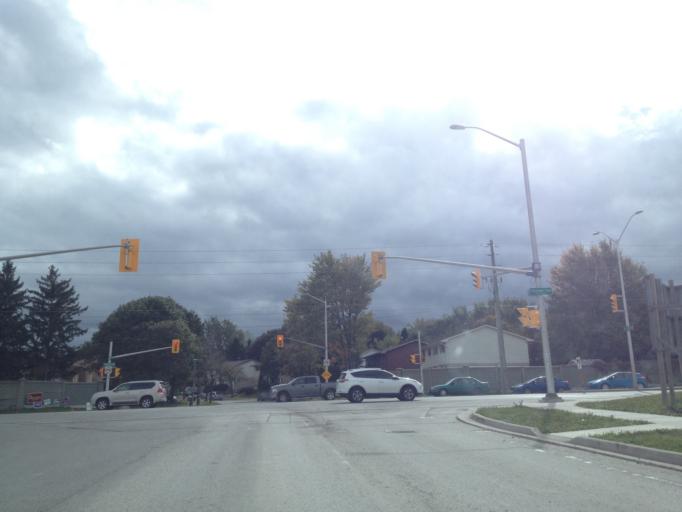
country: CA
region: Ontario
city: London
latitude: 43.0155
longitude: -81.3223
